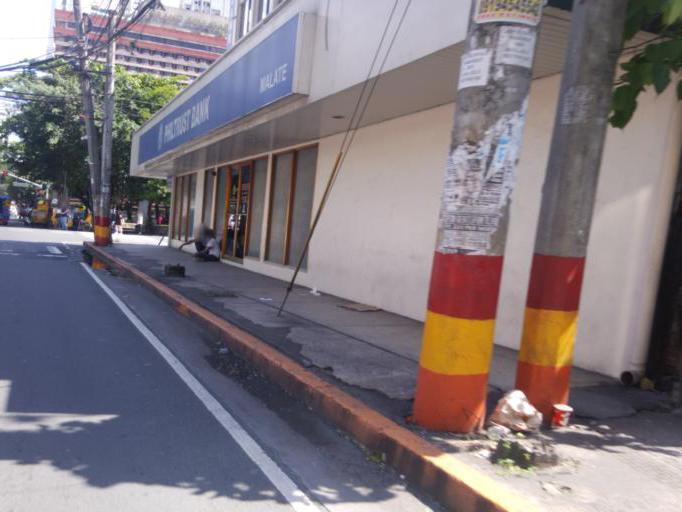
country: PH
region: Metro Manila
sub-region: City of Manila
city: Port Area
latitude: 14.5697
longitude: 120.9840
